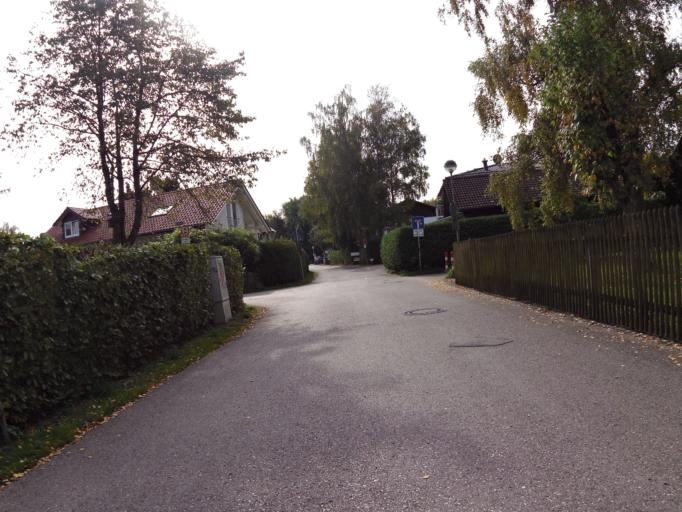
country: DE
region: Bavaria
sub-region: Upper Bavaria
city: Starnberg
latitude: 47.9981
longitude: 11.3583
